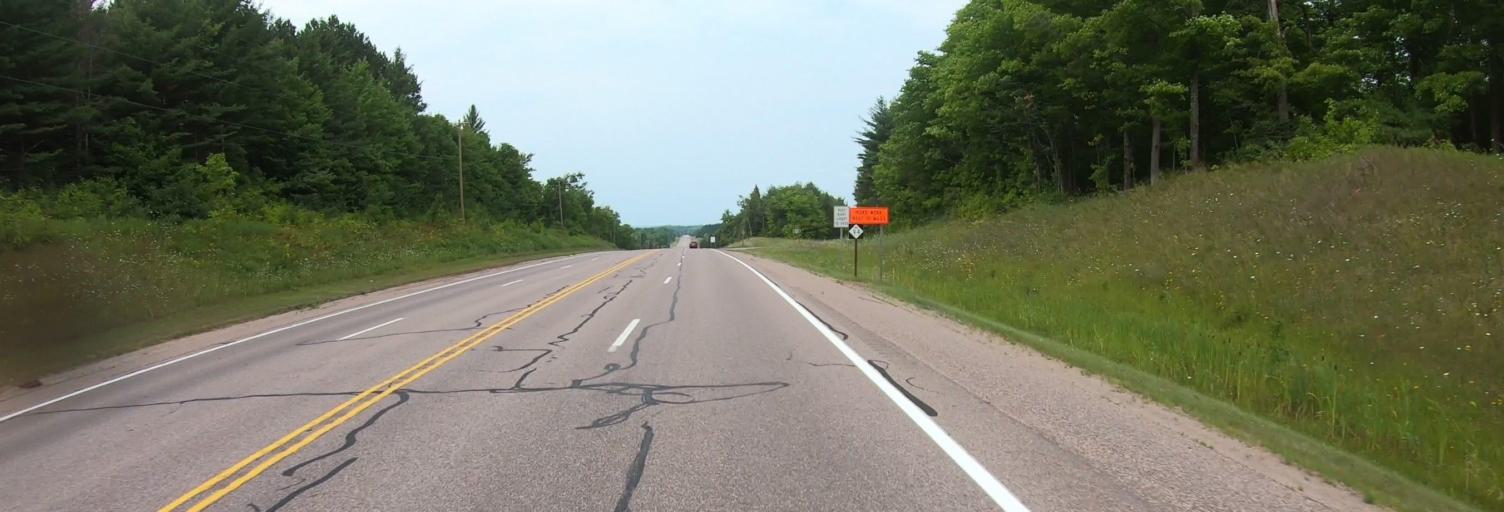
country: US
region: Michigan
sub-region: Marquette County
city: K. I. Sawyer Air Force Base
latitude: 46.3535
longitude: -87.2206
